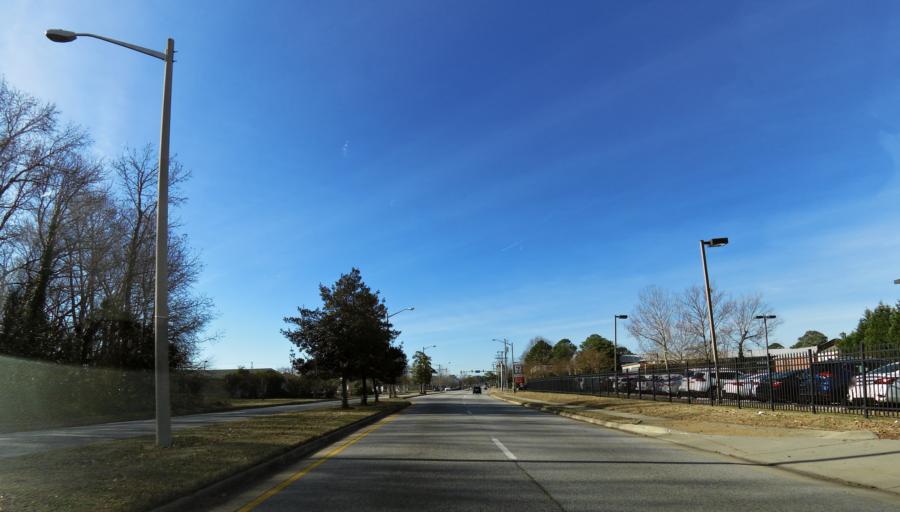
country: US
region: Virginia
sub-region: City of Hampton
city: Hampton
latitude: 37.0419
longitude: -76.4025
